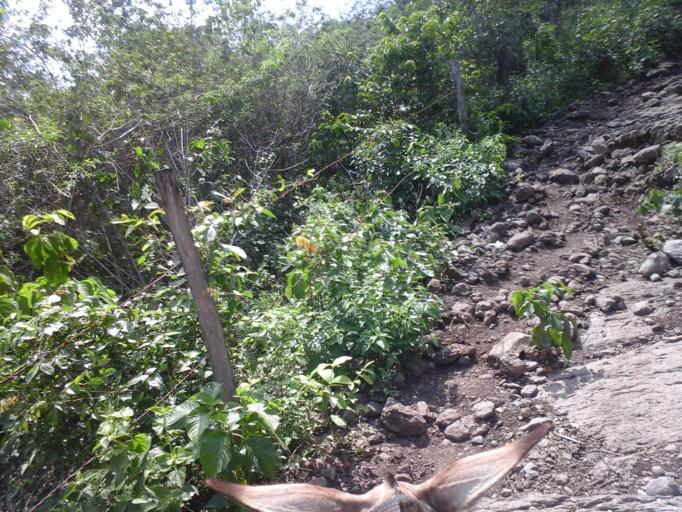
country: CO
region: Cesar
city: Becerril
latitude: 9.7512
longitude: -73.1391
